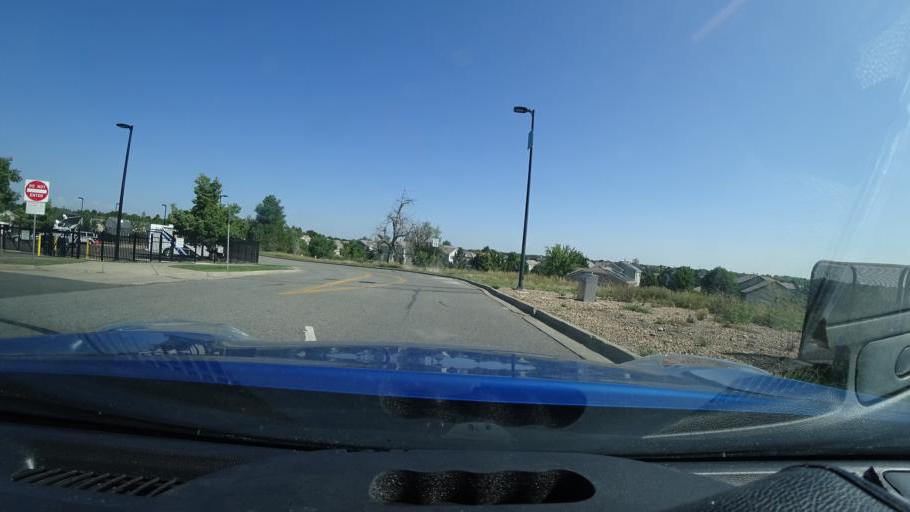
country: US
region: Colorado
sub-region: Adams County
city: Aurora
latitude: 39.7124
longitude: -104.8120
